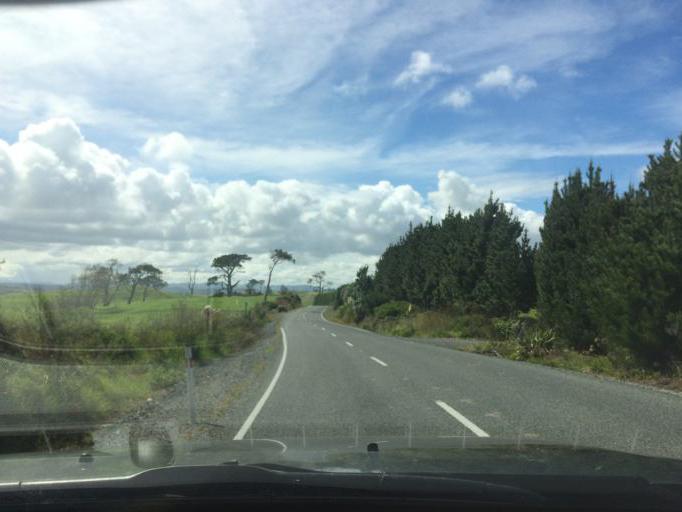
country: NZ
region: Northland
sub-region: Kaipara District
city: Dargaville
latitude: -35.9480
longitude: 173.7689
